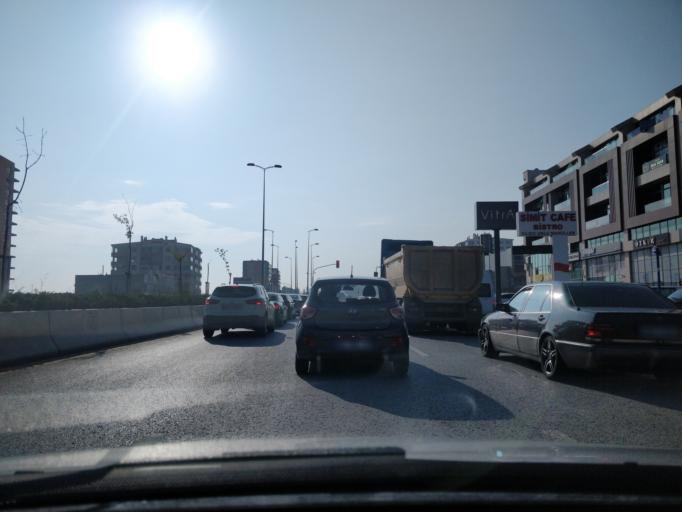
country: TR
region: Ankara
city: Etimesgut
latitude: 39.8974
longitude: 32.6507
